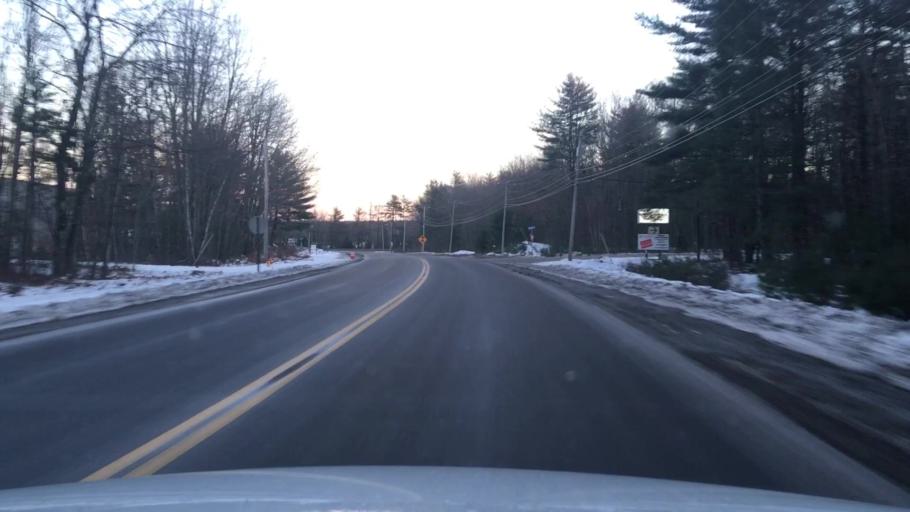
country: US
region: Maine
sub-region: Androscoggin County
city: Auburn
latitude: 44.0709
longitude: -70.2518
